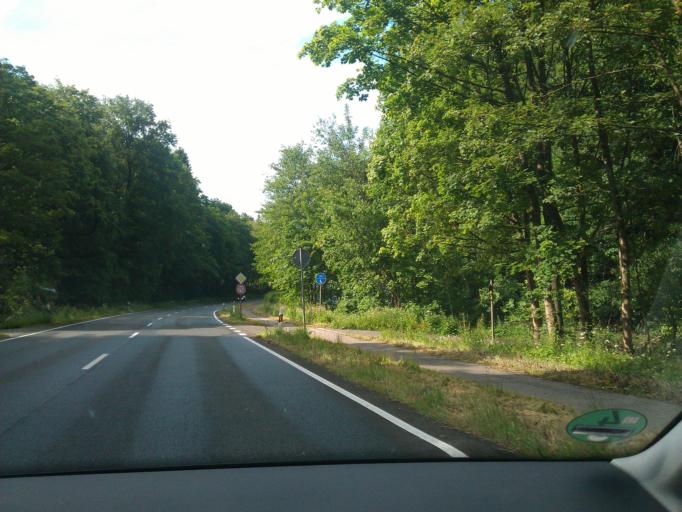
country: DE
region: North Rhine-Westphalia
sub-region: Regierungsbezirk Koln
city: Aachen
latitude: 50.7319
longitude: 6.0918
